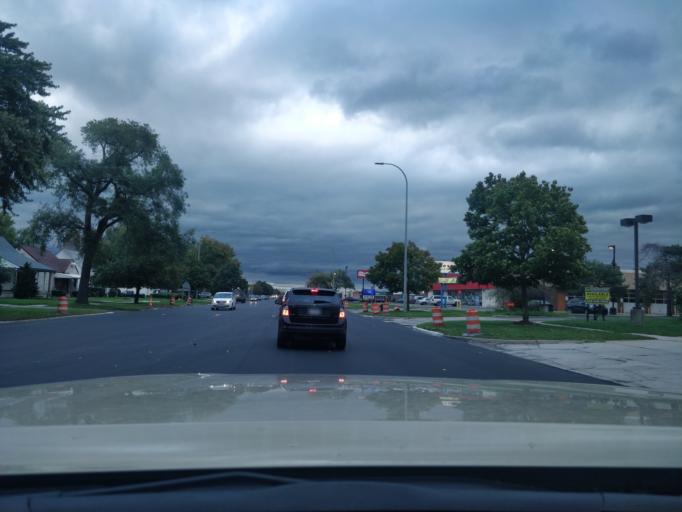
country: US
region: Michigan
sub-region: Wayne County
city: Southgate
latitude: 42.1991
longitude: -83.2045
